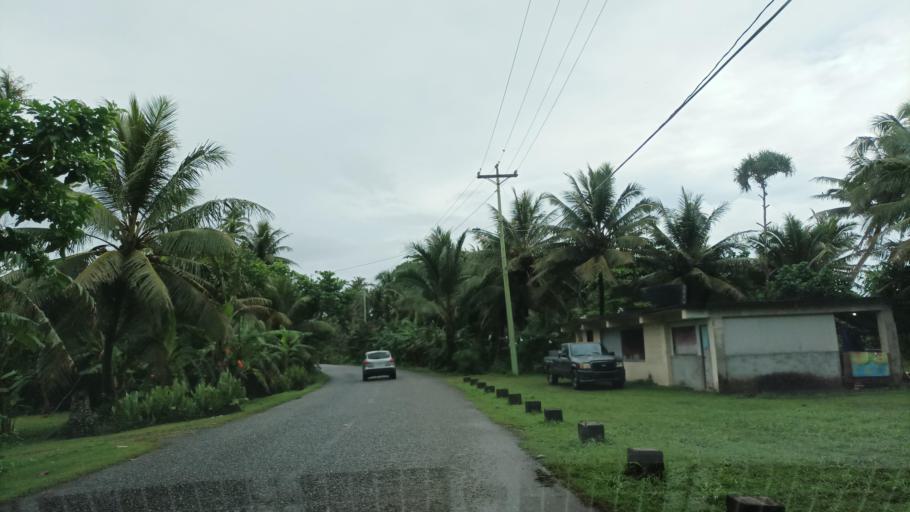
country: FM
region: Kosrae
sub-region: Lelu Municipality
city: Lelu
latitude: 5.3604
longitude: 163.0219
